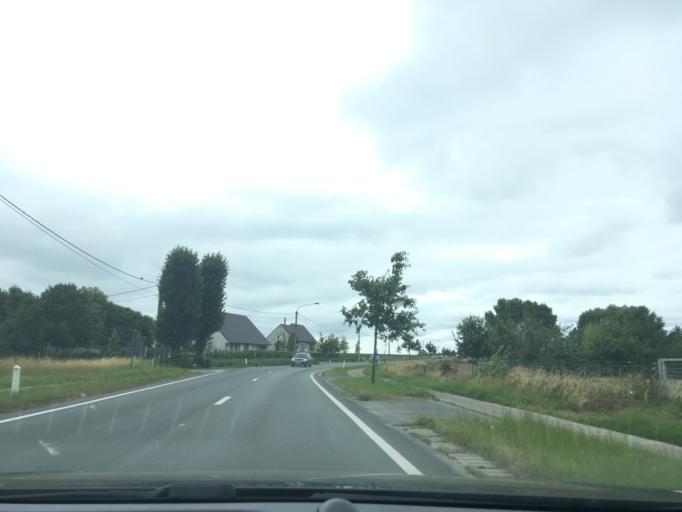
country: BE
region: Flanders
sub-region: Provincie West-Vlaanderen
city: Tielt
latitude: 51.0166
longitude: 3.3103
